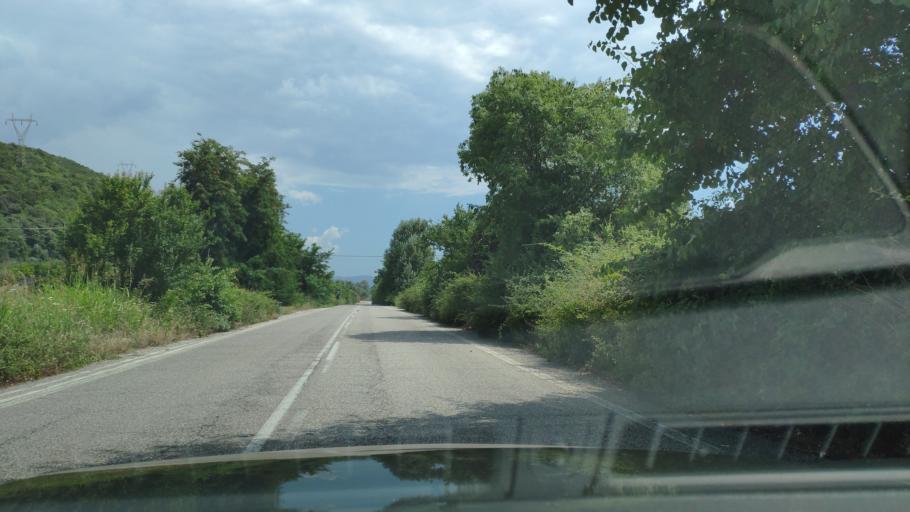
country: GR
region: West Greece
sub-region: Nomos Aitolias kai Akarnanias
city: Krikellos
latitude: 38.9876
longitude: 21.1614
